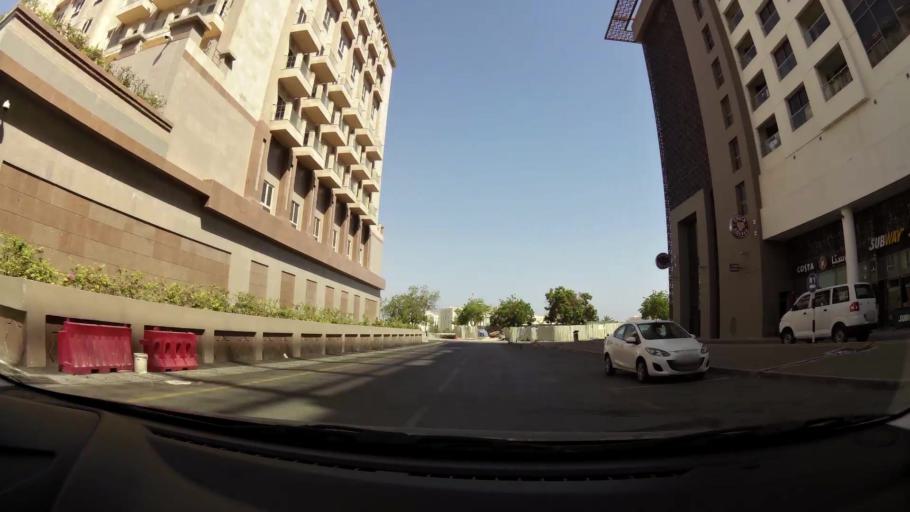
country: OM
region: Muhafazat Masqat
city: Bawshar
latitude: 23.5835
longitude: 58.4097
